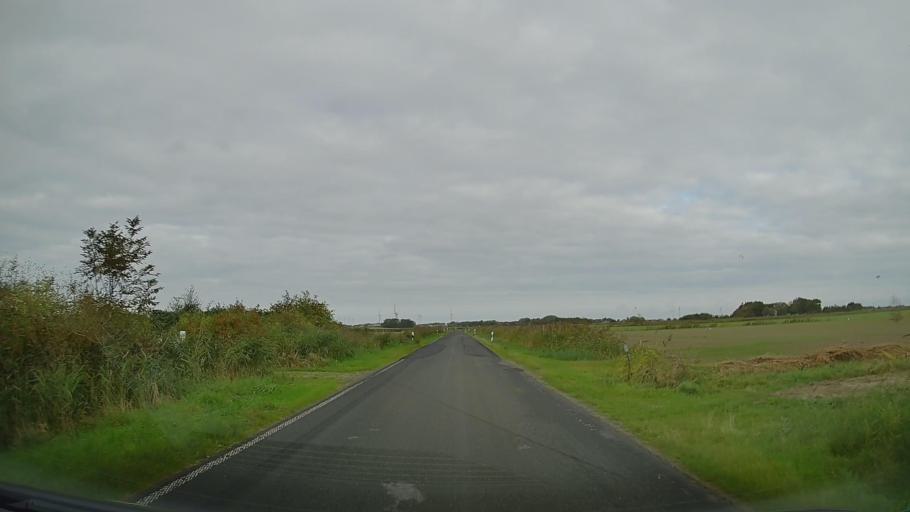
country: DE
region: Schleswig-Holstein
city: Emmelsbull-Horsbull
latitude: 54.8195
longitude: 8.6525
